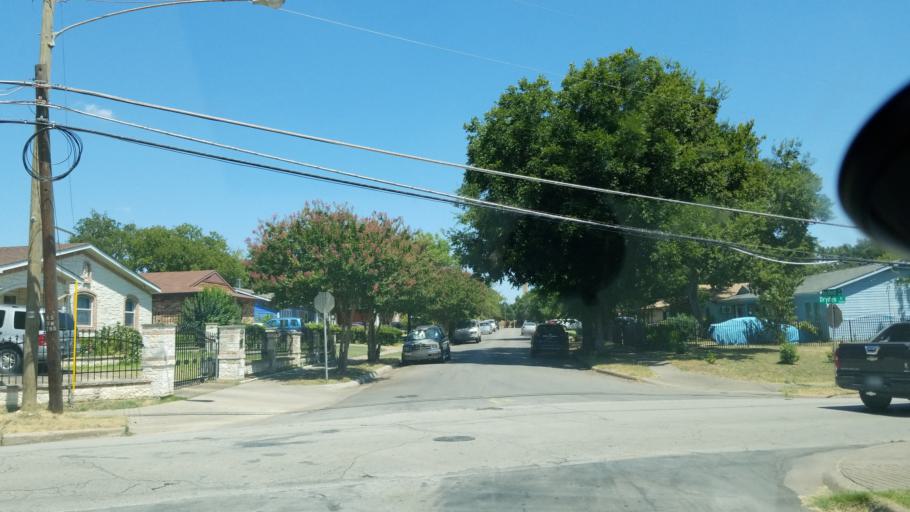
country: US
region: Texas
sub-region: Dallas County
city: Cockrell Hill
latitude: 32.7218
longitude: -96.8843
